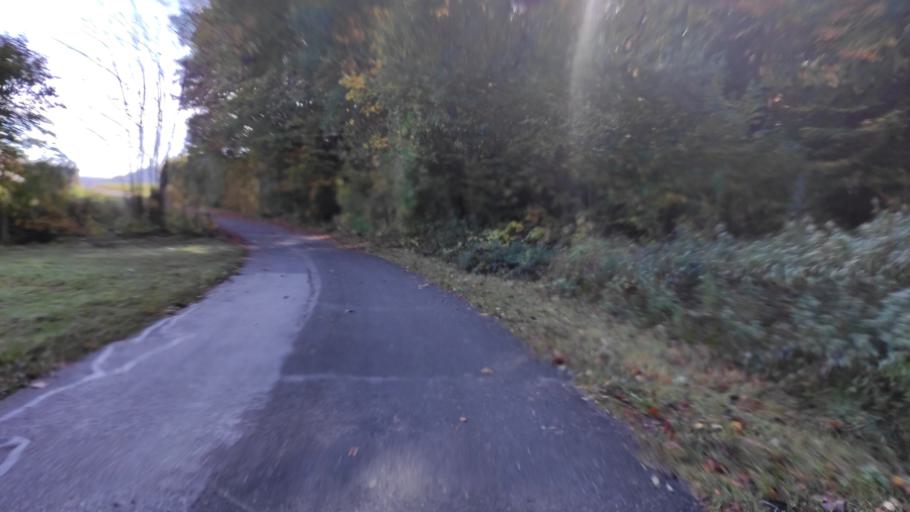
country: AT
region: Salzburg
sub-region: Politischer Bezirk Salzburg-Umgebung
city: Fuschl am See
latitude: 47.7952
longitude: 13.2772
